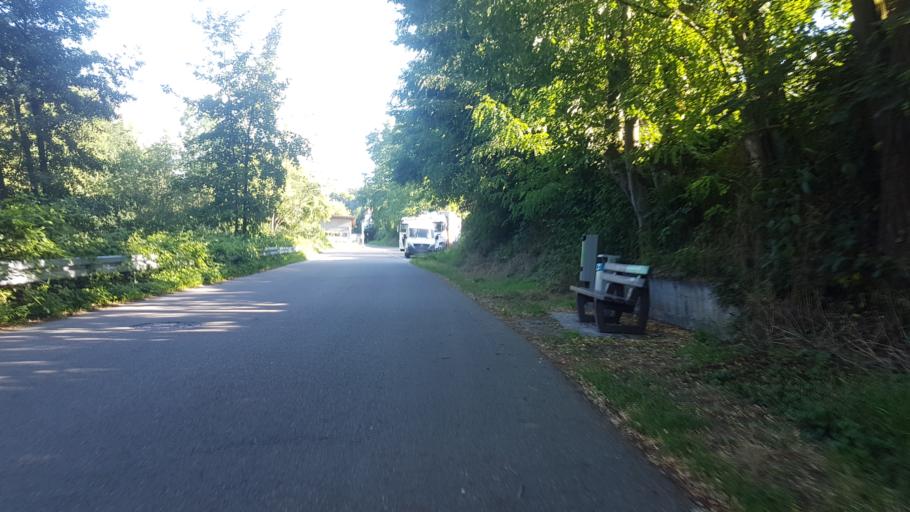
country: DE
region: Baden-Wuerttemberg
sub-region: Regierungsbezirk Stuttgart
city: Mockmuhl
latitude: 49.3187
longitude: 9.3586
